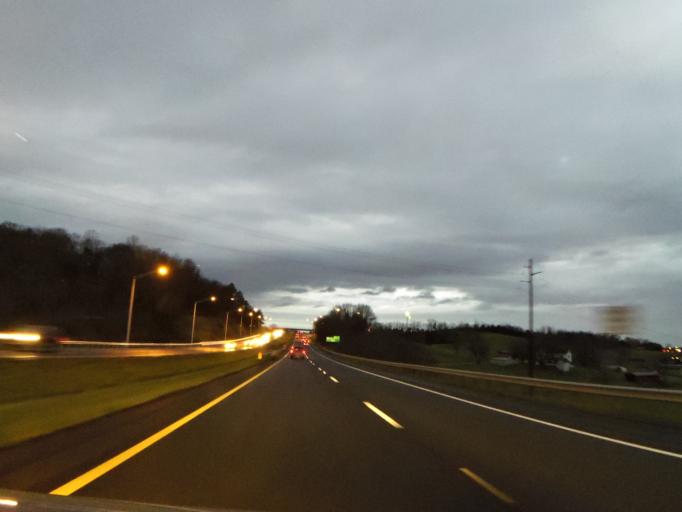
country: US
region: Tennessee
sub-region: Washington County
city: Gray
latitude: 36.4030
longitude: -82.4695
